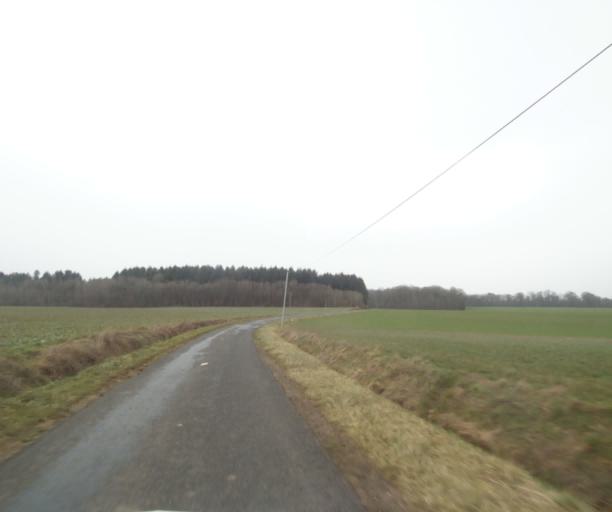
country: FR
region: Champagne-Ardenne
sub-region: Departement de la Haute-Marne
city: Chevillon
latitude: 48.4954
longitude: 5.0594
